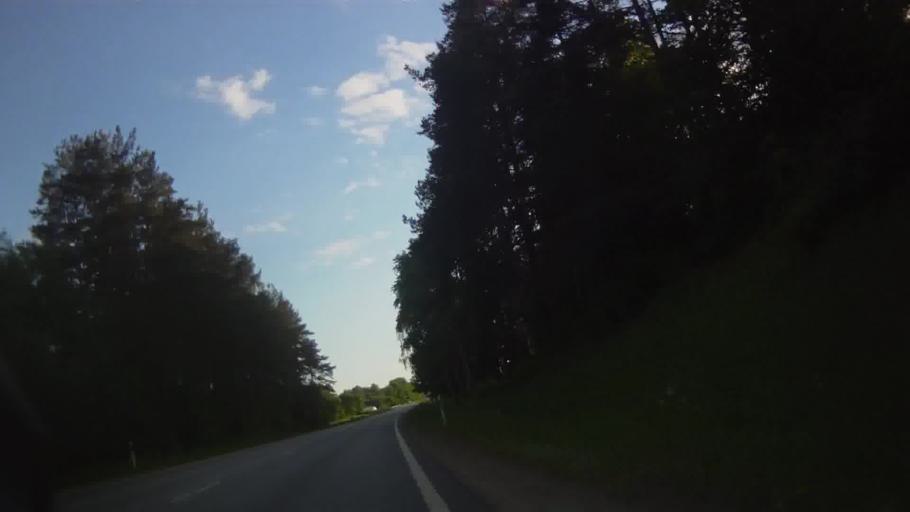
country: LV
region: Varaklani
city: Varaklani
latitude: 56.5698
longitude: 26.6483
